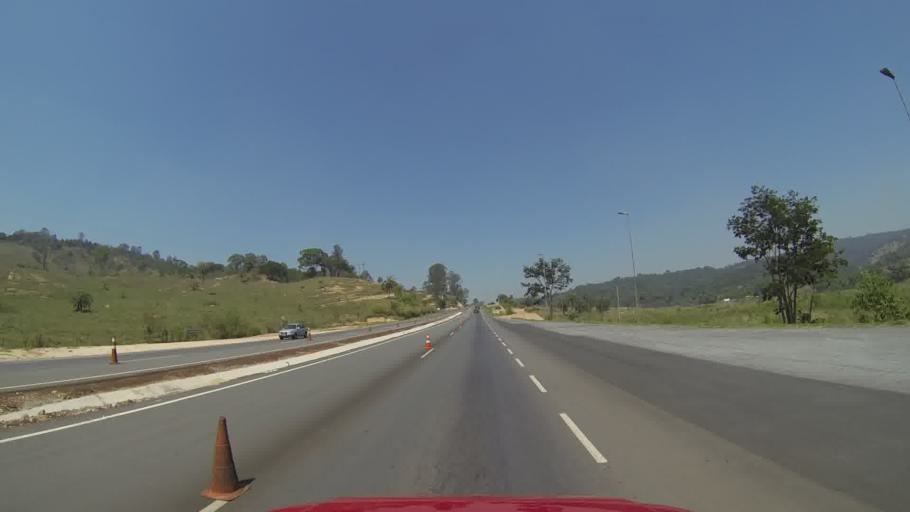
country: BR
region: Minas Gerais
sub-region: Mateus Leme
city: Mateus Leme
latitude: -20.0185
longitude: -44.4945
